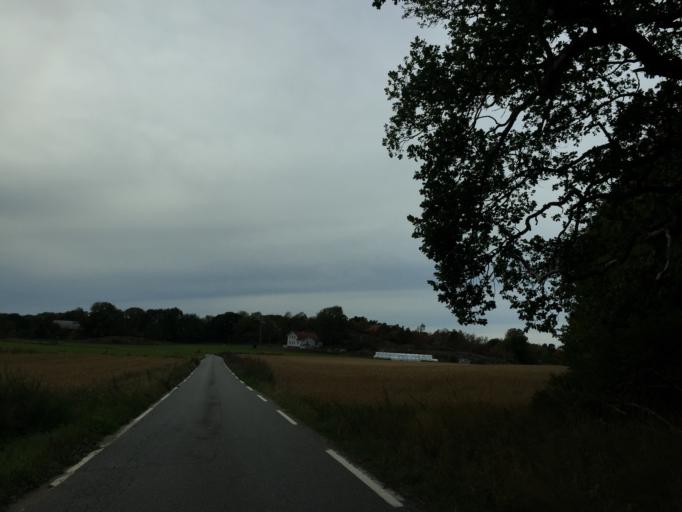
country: NO
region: Ostfold
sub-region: Hvaler
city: Skjaerhalden
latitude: 59.0391
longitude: 11.0460
